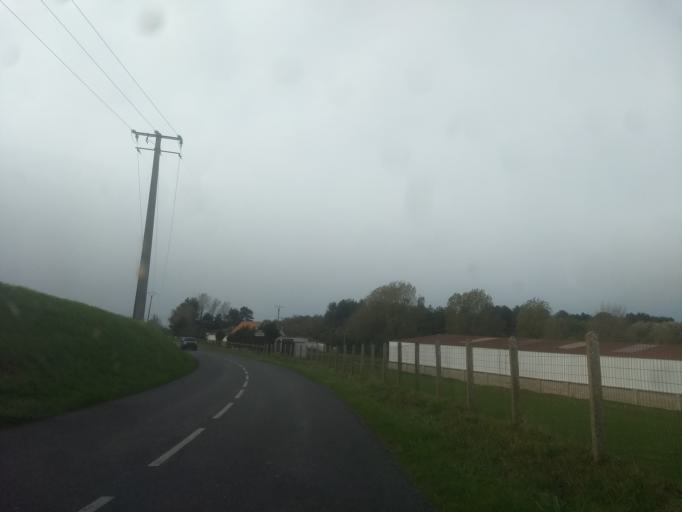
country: FR
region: Nord-Pas-de-Calais
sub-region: Departement du Pas-de-Calais
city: Wissant
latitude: 50.8899
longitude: 1.6800
